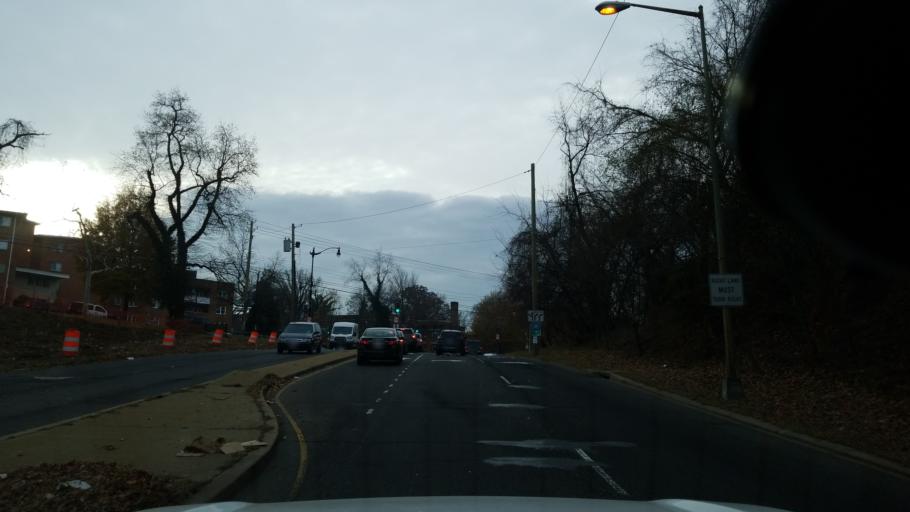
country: US
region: Maryland
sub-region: Prince George's County
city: Glassmanor
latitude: 38.8363
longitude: -77.0089
